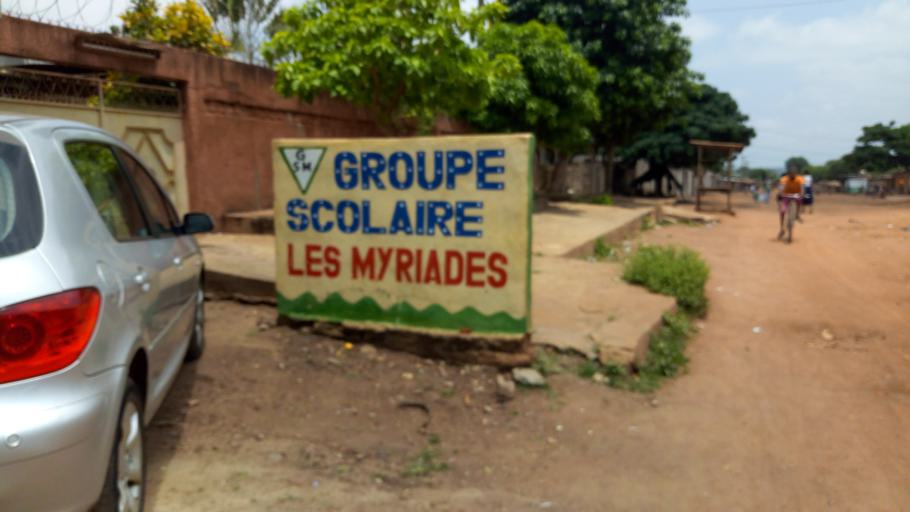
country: CI
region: Vallee du Bandama
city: Bouake
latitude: 7.7214
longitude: -4.9985
